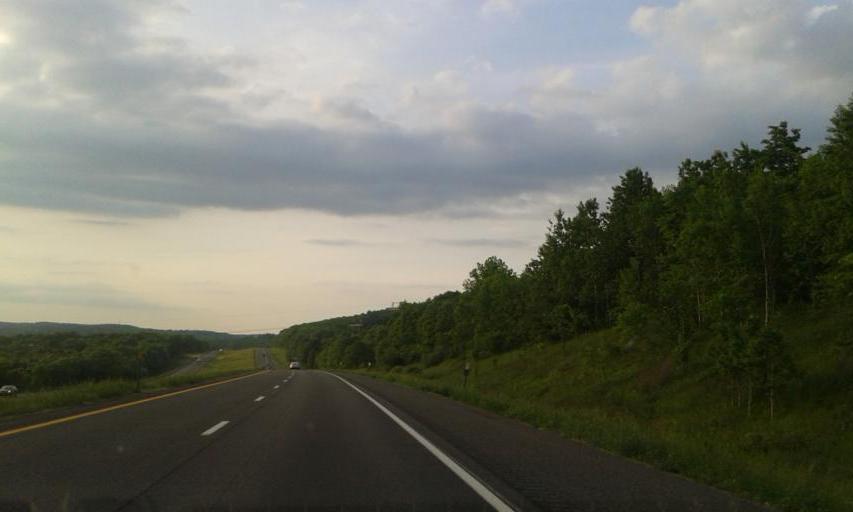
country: US
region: New York
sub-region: Broome County
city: Chenango Bridge
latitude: 42.2061
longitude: -75.8993
